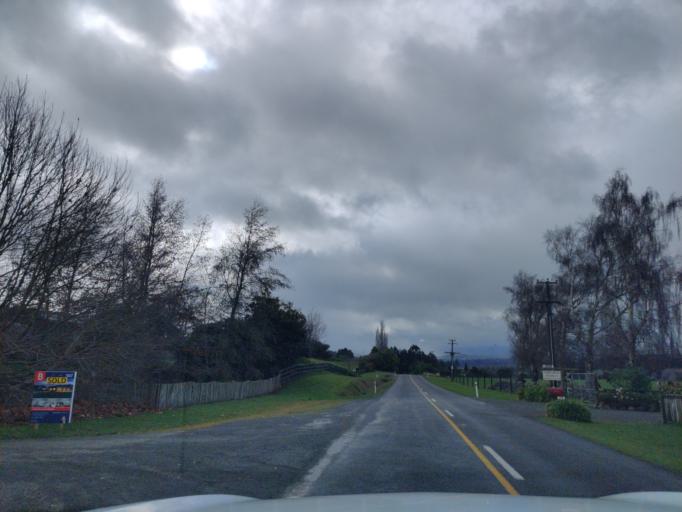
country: NZ
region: Manawatu-Wanganui
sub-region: Palmerston North City
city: Palmerston North
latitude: -40.1854
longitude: 175.7849
